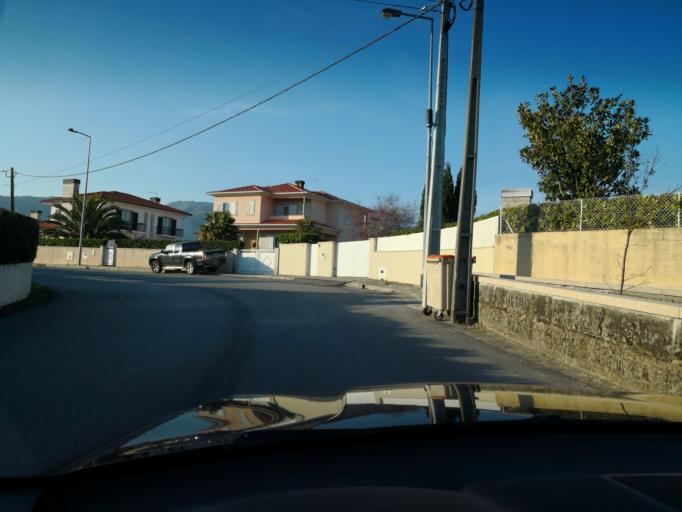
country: PT
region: Vila Real
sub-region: Vila Real
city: Vila Real
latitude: 41.2967
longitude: -7.7658
